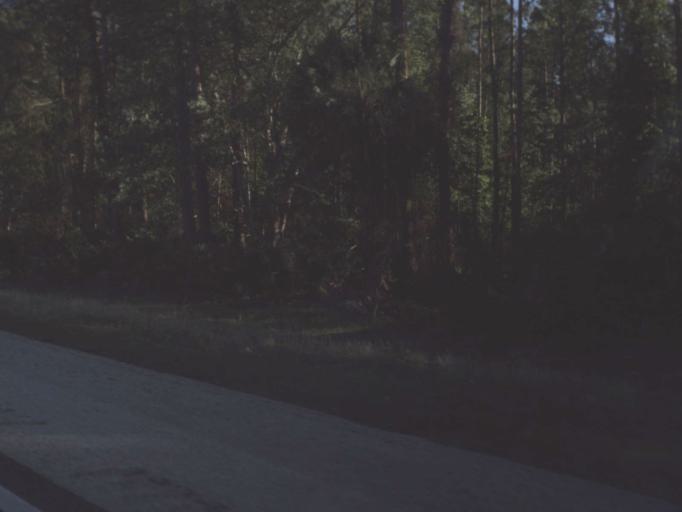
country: US
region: Florida
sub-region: Flagler County
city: Palm Coast
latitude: 29.6392
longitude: -81.2698
